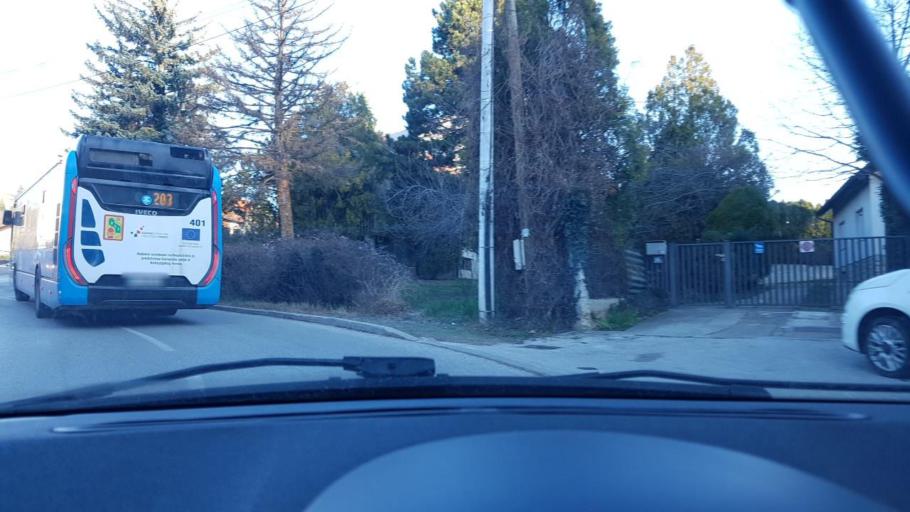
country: HR
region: Grad Zagreb
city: Zagreb
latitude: 45.8493
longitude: 15.9855
